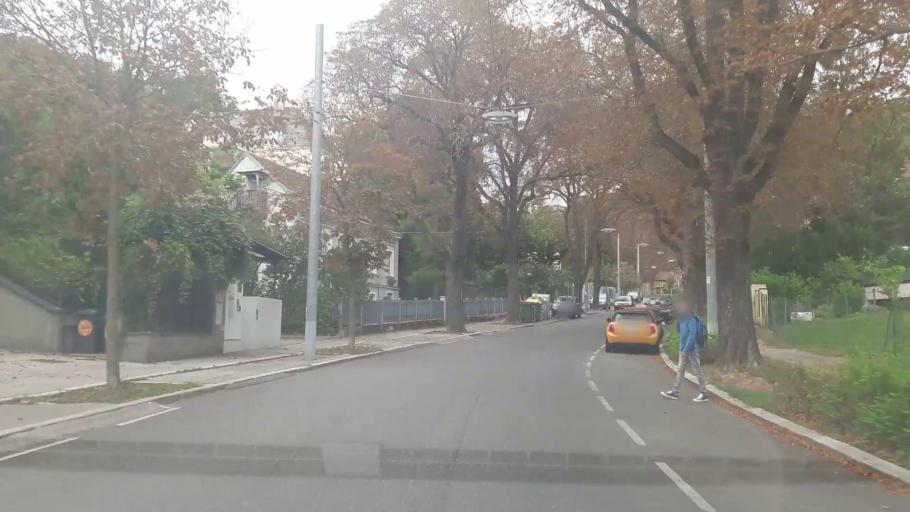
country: AT
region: Lower Austria
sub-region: Politischer Bezirk Korneuburg
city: Langenzersdorf
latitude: 48.2613
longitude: 16.3326
